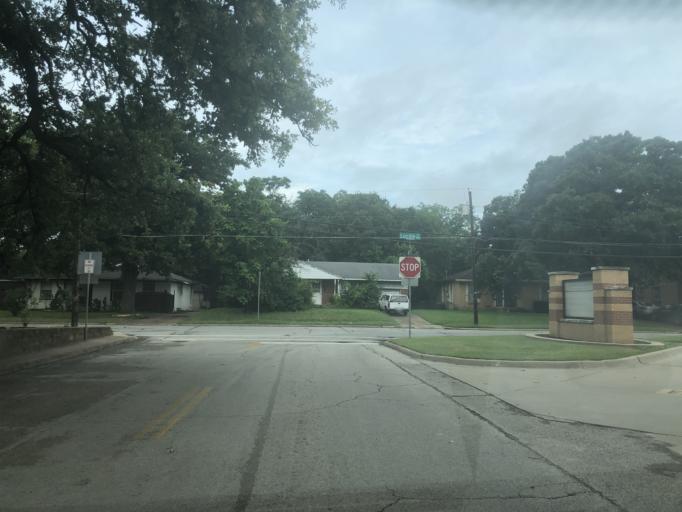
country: US
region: Texas
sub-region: Dallas County
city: Irving
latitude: 32.8049
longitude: -96.9400
